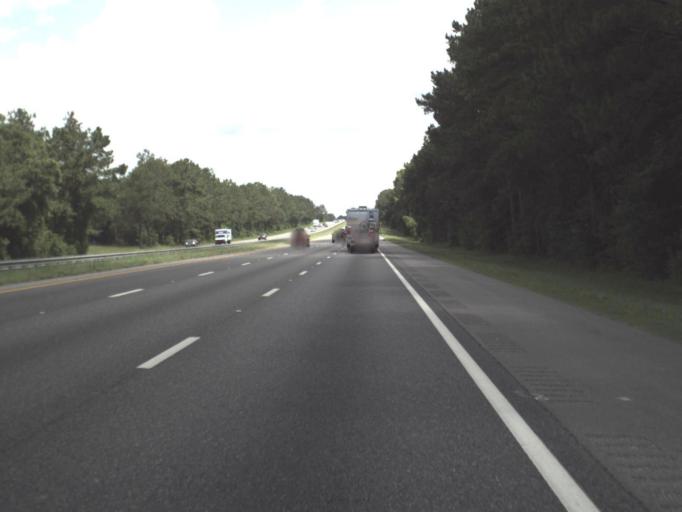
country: US
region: Florida
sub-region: Columbia County
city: Lake City
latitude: 30.0368
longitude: -82.6160
